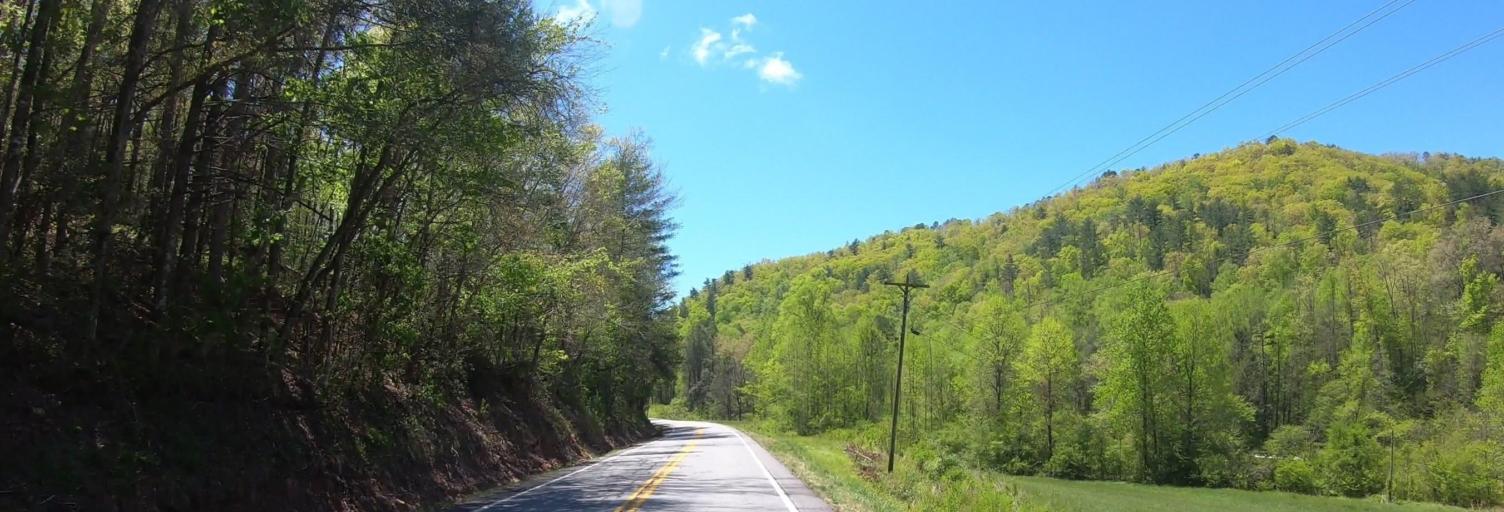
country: US
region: Georgia
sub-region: White County
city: Cleveland
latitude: 34.7622
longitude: -83.7495
